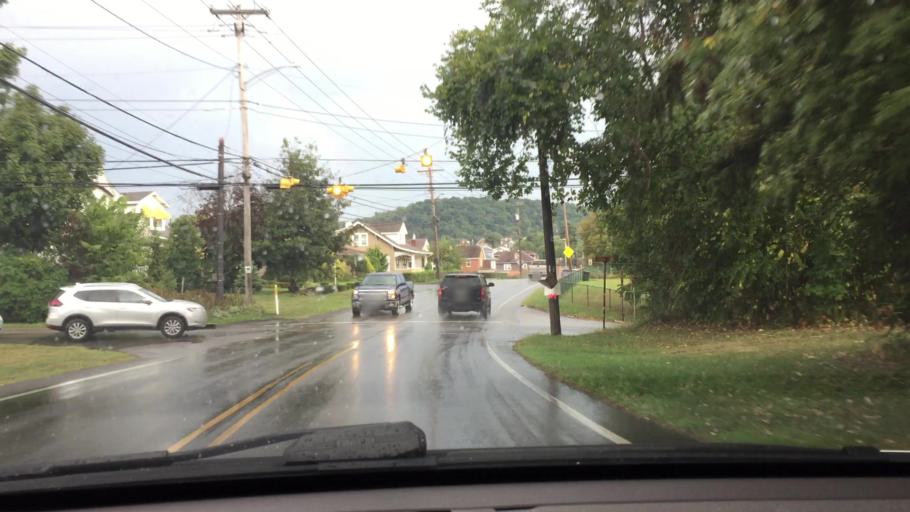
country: US
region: Pennsylvania
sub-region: Washington County
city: Canonsburg
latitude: 40.2689
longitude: -80.1826
